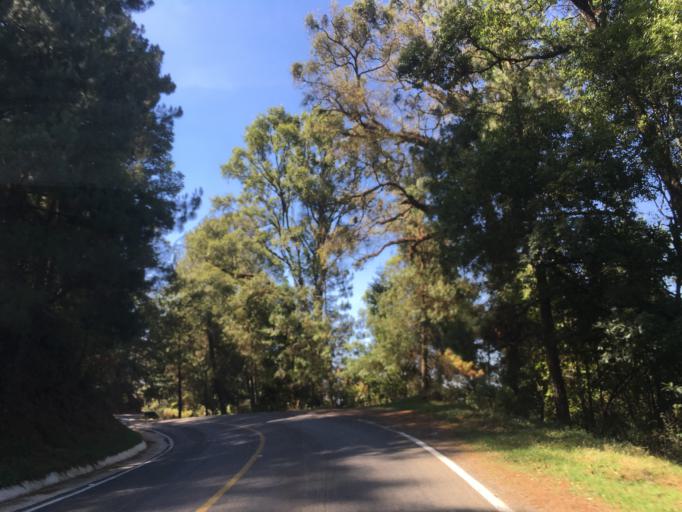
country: MX
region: Michoacan
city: Tzitzio
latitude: 19.6824
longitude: -100.8957
